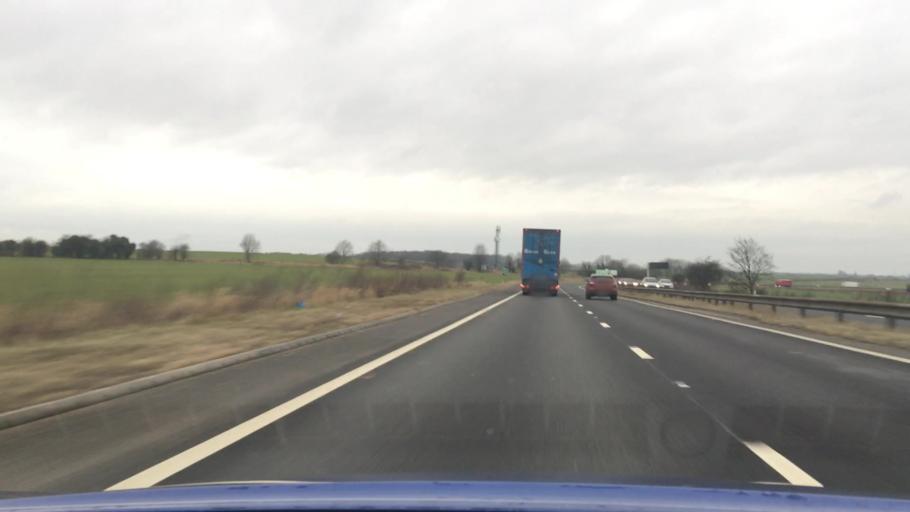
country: GB
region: England
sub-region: City and Borough of Wakefield
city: Darrington
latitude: 53.6562
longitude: -1.2620
